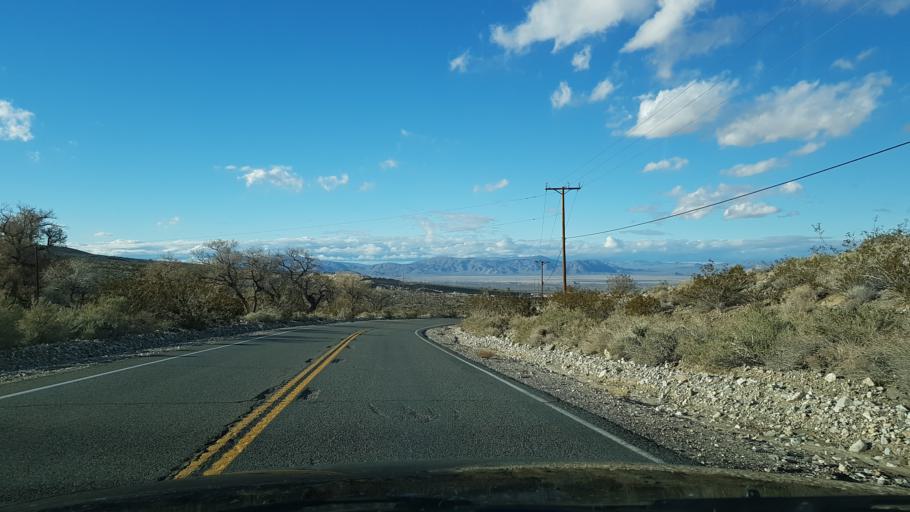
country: US
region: California
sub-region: San Bernardino County
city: Big Bear City
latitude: 34.3633
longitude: -116.8571
